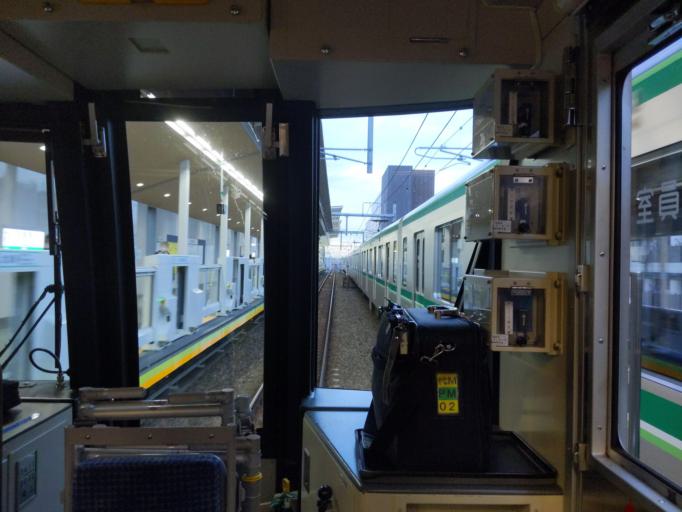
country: JP
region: Saitama
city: Yashio-shi
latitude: 35.7762
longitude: 139.8321
